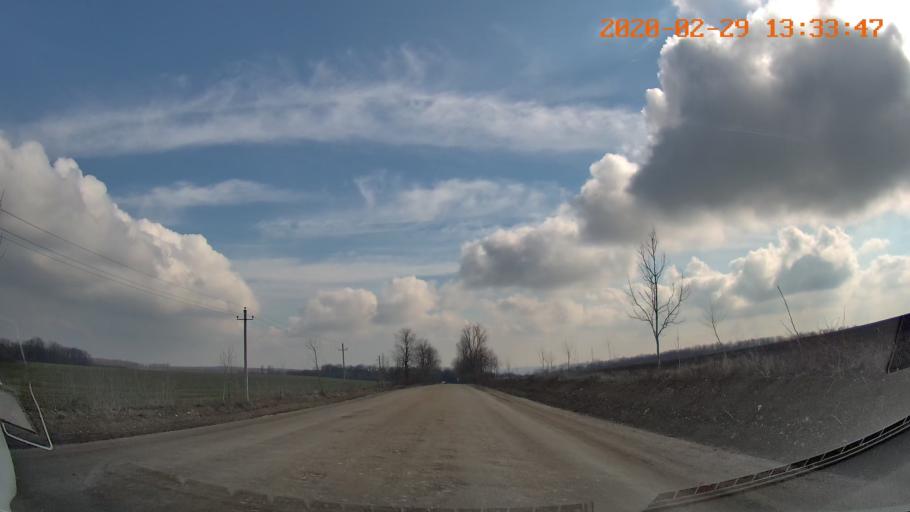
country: MD
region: Telenesti
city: Camenca
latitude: 47.8719
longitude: 28.6187
